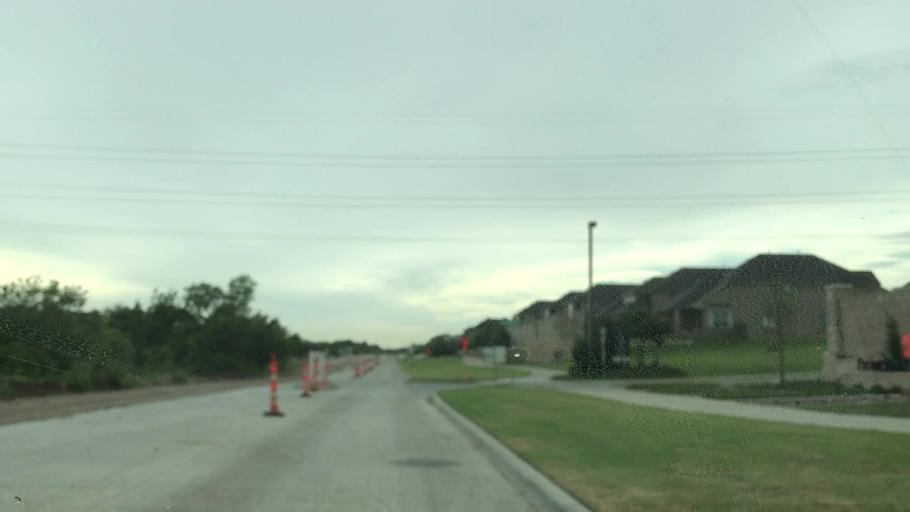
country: US
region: Texas
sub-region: Dallas County
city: Coppell
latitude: 32.9031
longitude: -96.9948
